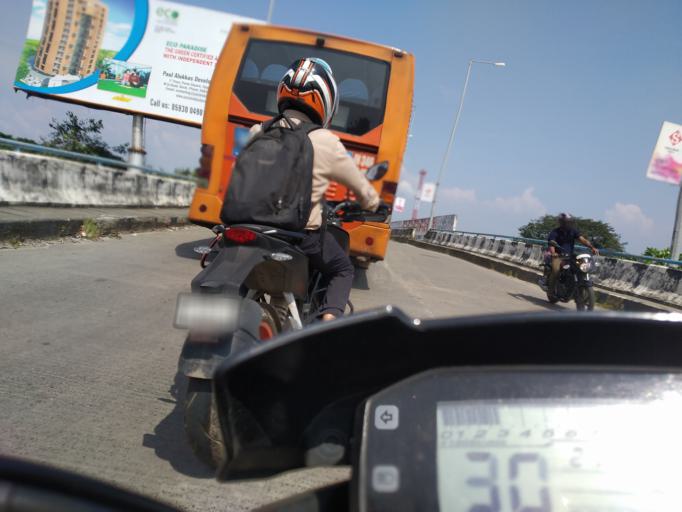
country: IN
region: Kerala
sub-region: Ernakulam
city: Cochin
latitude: 9.9763
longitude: 76.2892
